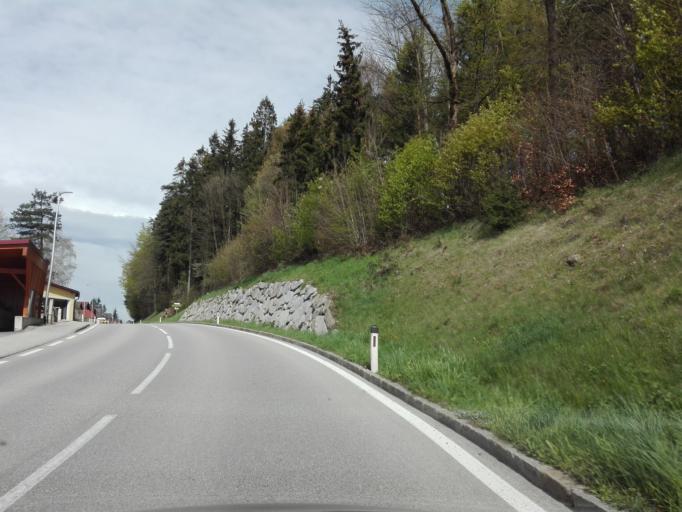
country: AT
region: Upper Austria
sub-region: Politischer Bezirk Urfahr-Umgebung
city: Eidenberg
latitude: 48.3468
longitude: 14.2439
